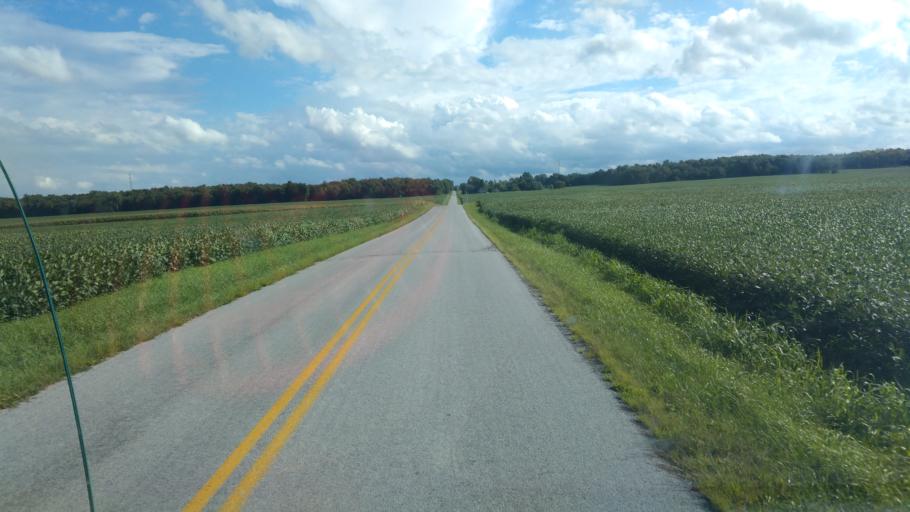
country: US
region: Ohio
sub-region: Hardin County
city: Kenton
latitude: 40.6767
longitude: -83.6338
